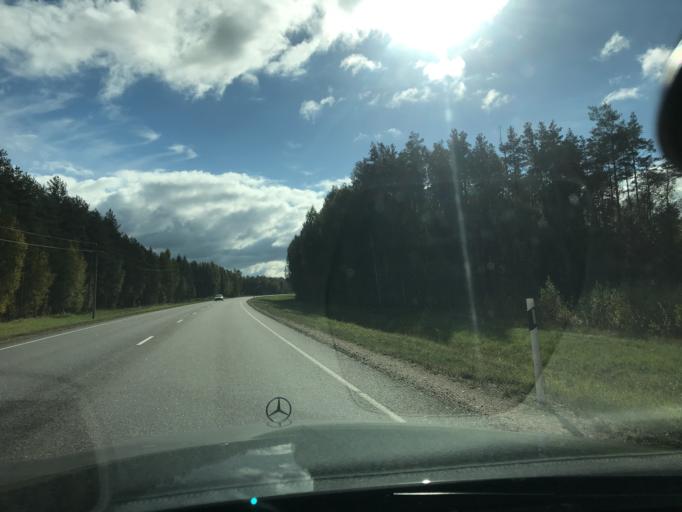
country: EE
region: Vorumaa
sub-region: Voru linn
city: Voru
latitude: 57.8378
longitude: 27.0572
